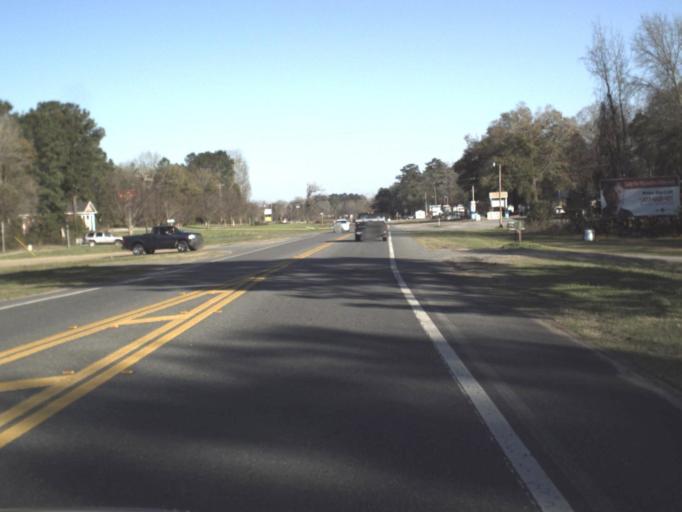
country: US
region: Florida
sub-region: Jackson County
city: Sneads
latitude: 30.7107
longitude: -84.9166
